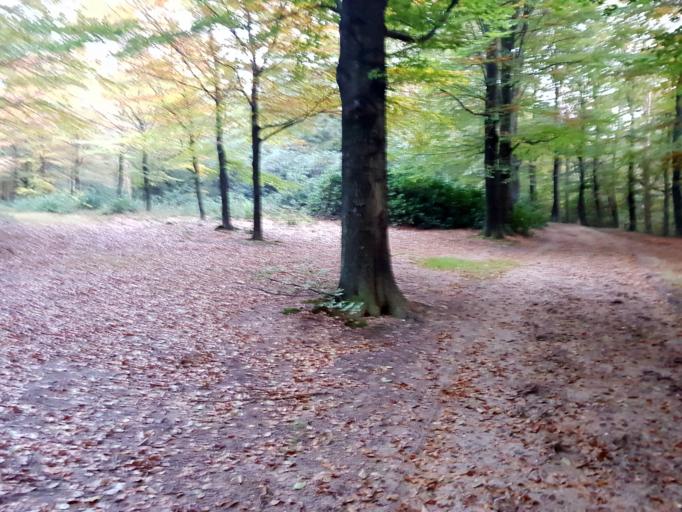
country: NL
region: Utrecht
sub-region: Gemeente Utrechtse Heuvelrug
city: Maarsbergen
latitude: 52.0404
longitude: 5.4025
